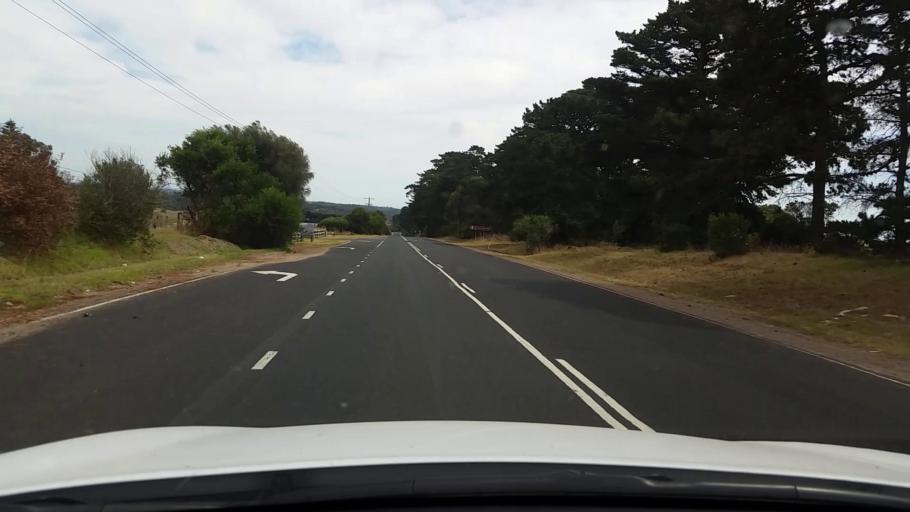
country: AU
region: Victoria
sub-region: Mornington Peninsula
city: Rosebud West
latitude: -38.4318
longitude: 144.8935
